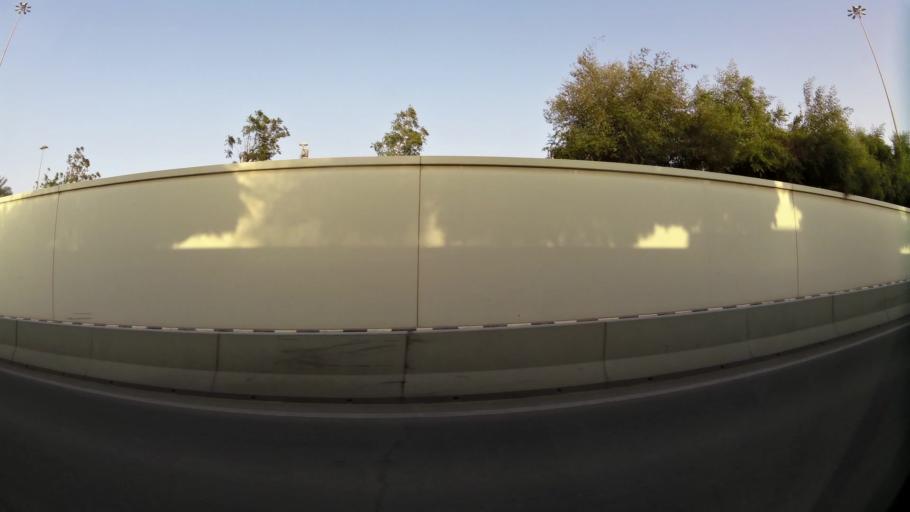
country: QA
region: Baladiyat ar Rayyan
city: Ar Rayyan
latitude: 25.3192
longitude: 51.4601
